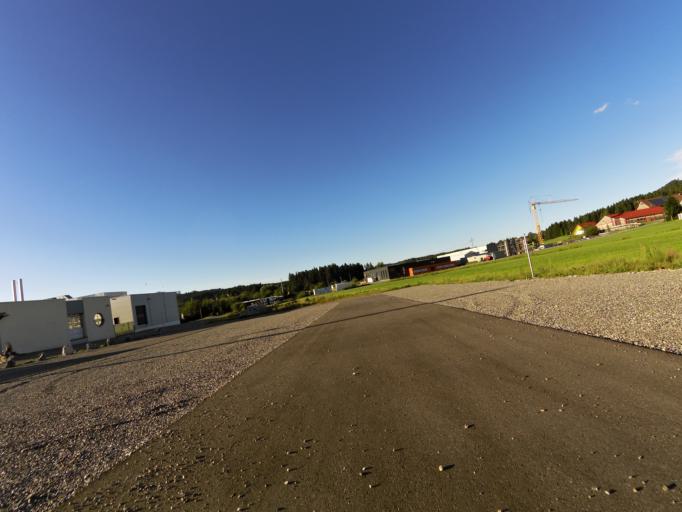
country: DE
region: Bavaria
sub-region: Swabia
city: Weiler-Simmerberg
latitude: 47.5858
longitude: 9.9207
